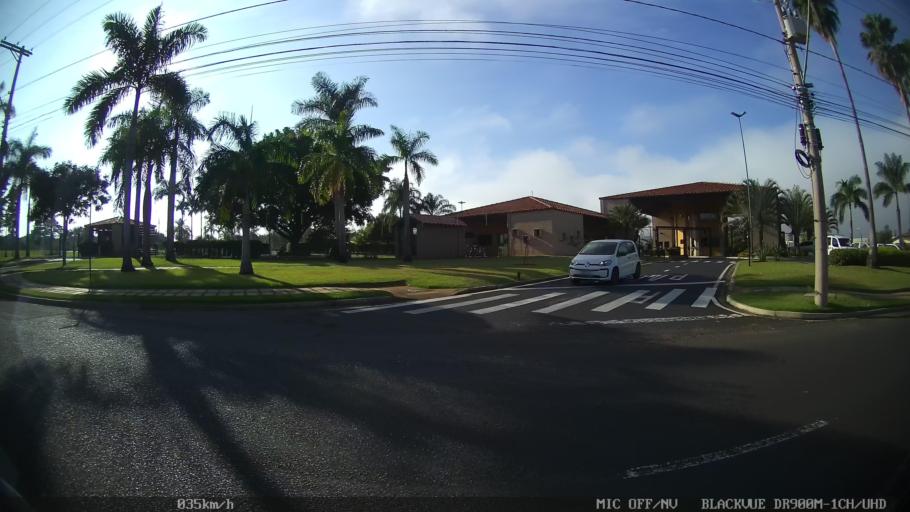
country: BR
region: Sao Paulo
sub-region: Sao Jose Do Rio Preto
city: Sao Jose do Rio Preto
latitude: -20.8172
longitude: -49.3384
